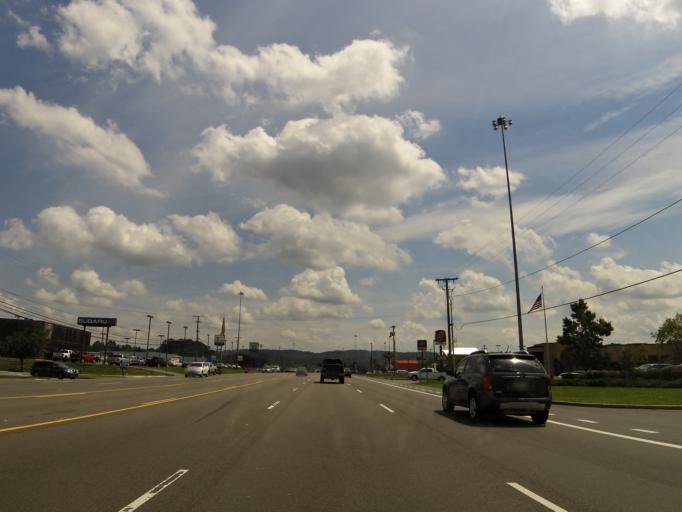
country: US
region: Tennessee
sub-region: Sullivan County
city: Kingsport
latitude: 36.5517
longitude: -82.5292
